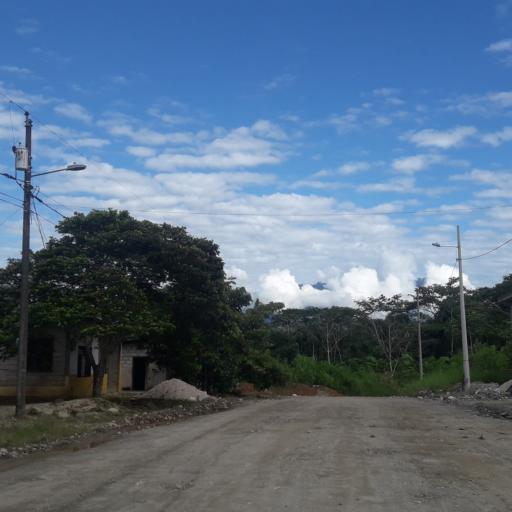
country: EC
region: Napo
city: Tena
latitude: -0.9832
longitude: -77.8259
